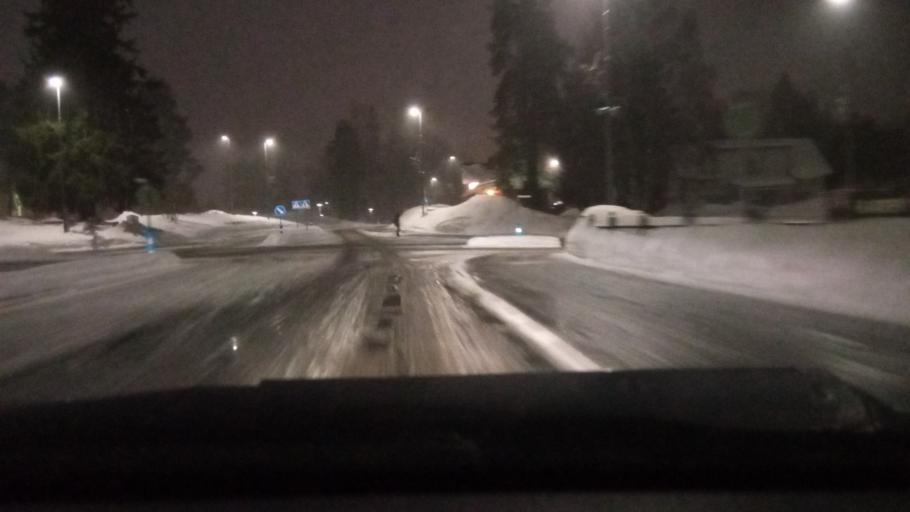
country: FI
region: Southern Ostrobothnia
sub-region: Jaerviseutu
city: Alajaervi
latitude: 63.0003
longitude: 23.8157
